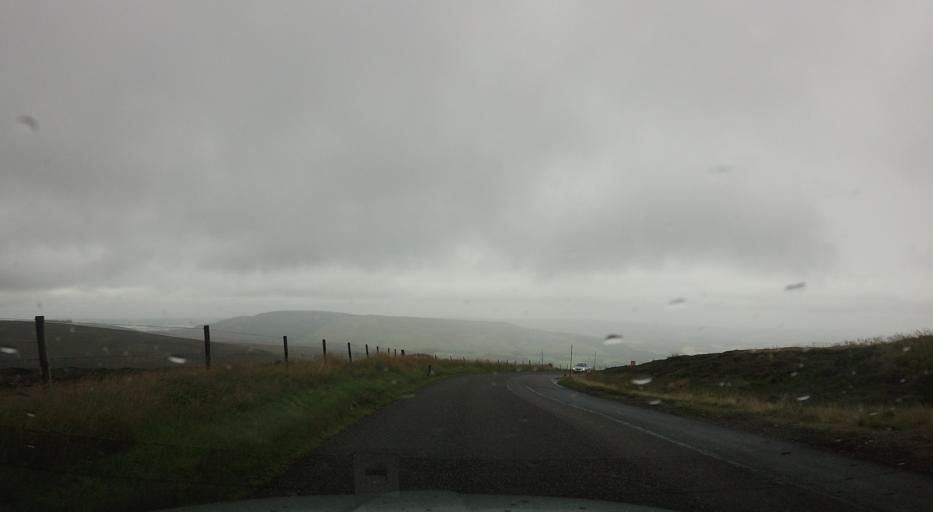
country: GB
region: Scotland
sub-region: Aberdeenshire
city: Laurencekirk
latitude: 56.9163
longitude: -2.5766
